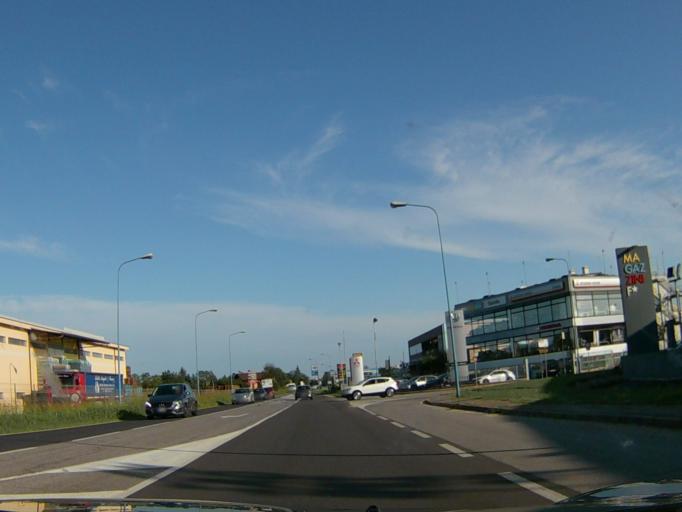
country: IT
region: Lombardy
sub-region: Provincia di Brescia
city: Molinetto
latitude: 45.4914
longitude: 10.3635
